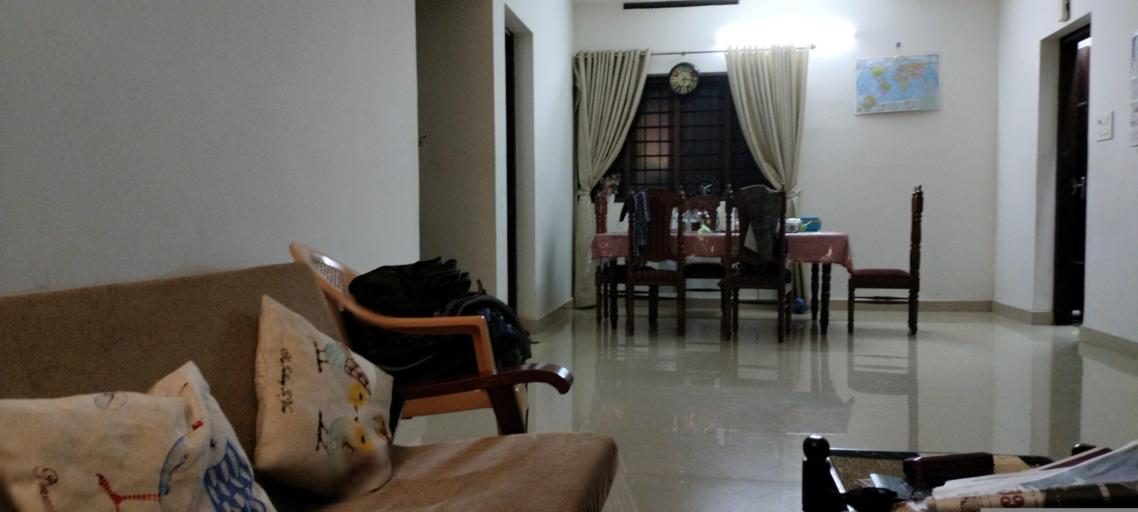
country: IN
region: Kerala
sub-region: Kottayam
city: Changanacheri
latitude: 9.4318
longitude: 76.5394
